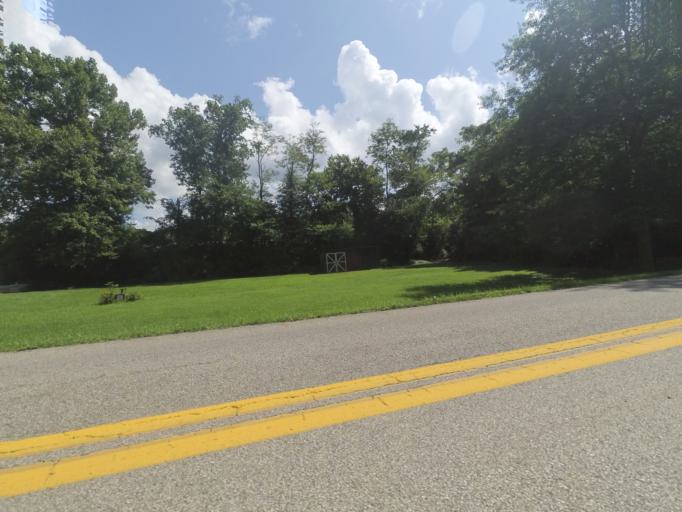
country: US
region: West Virginia
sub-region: Cabell County
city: Pea Ridge
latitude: 38.4260
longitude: -82.3307
